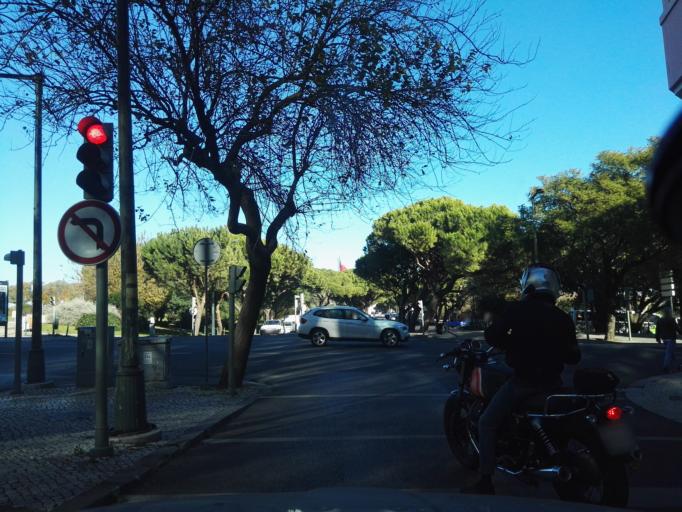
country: PT
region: Lisbon
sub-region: Lisbon
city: Lisbon
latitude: 38.7293
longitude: -9.1576
